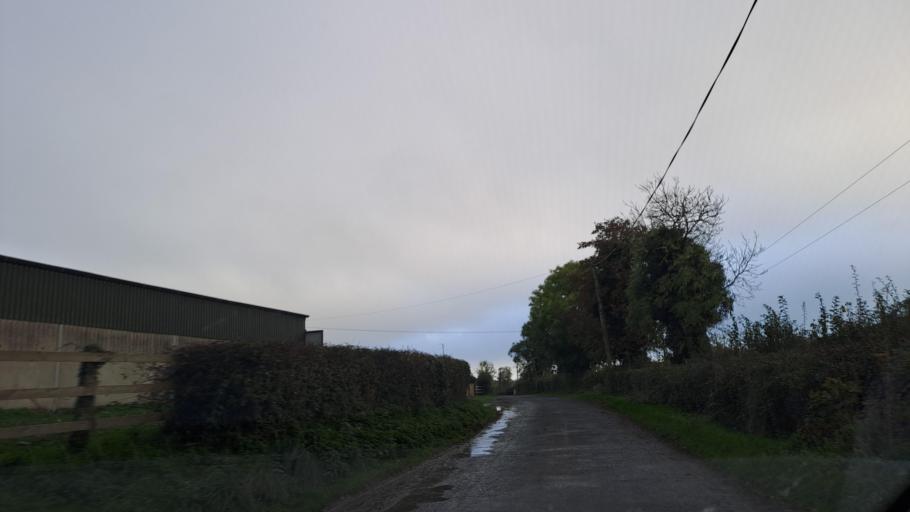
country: IE
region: Ulster
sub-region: County Monaghan
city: Carrickmacross
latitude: 53.9773
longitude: -6.6734
